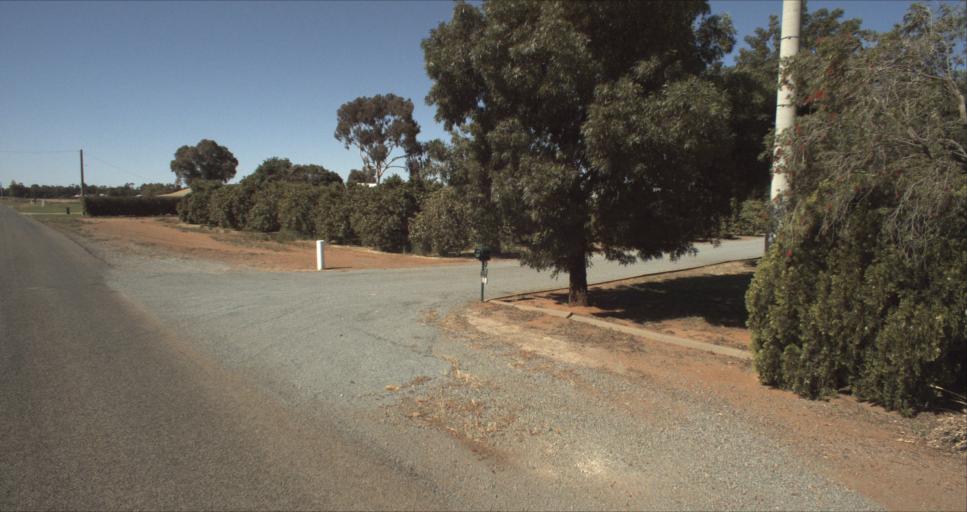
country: AU
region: New South Wales
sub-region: Leeton
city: Leeton
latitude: -34.5651
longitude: 146.3828
